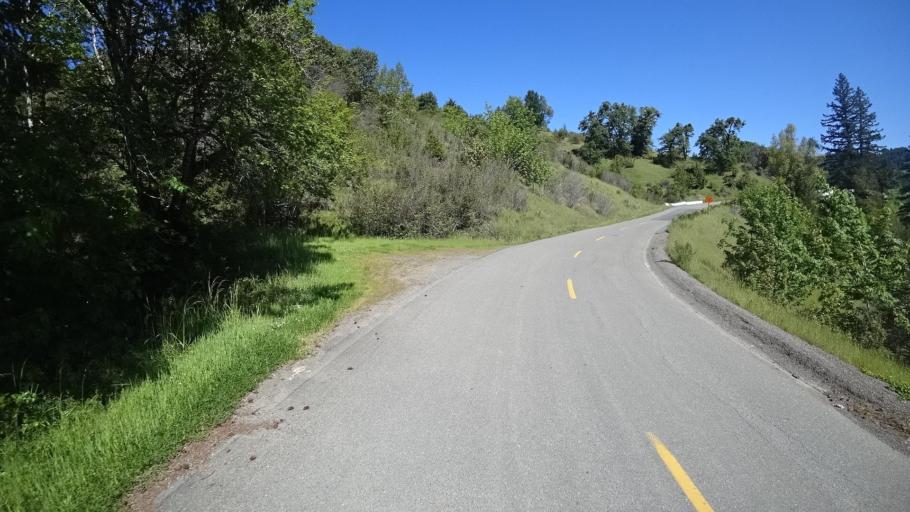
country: US
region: California
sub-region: Humboldt County
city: Rio Dell
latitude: 40.2521
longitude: -124.1900
